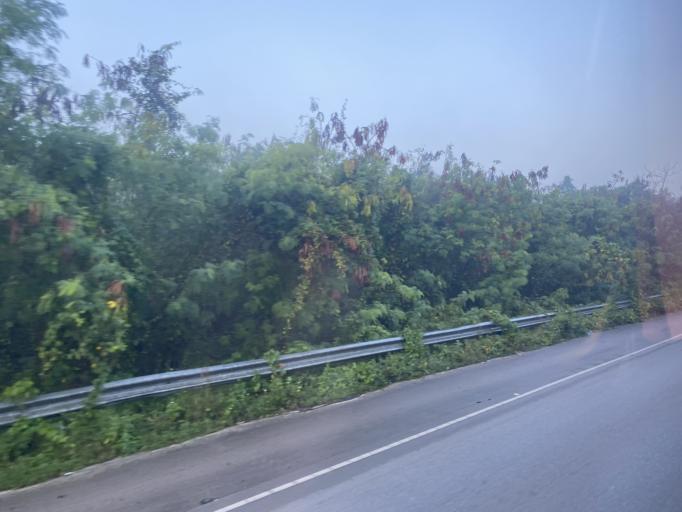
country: DO
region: La Altagracia
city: Otra Banda
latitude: 18.7380
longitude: -68.5123
